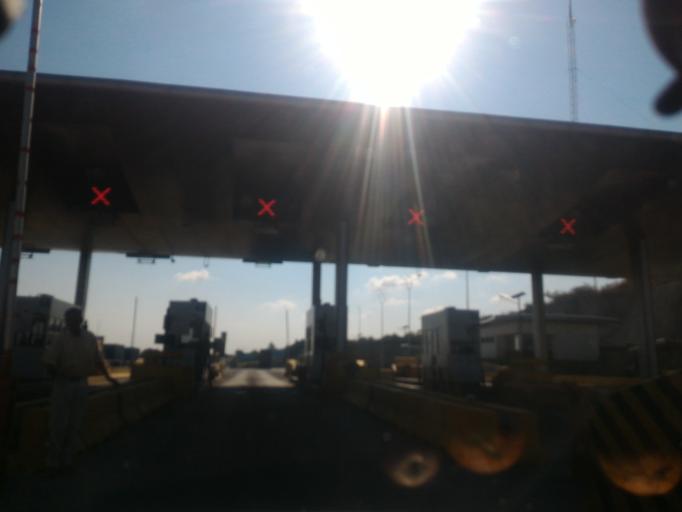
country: MX
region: Jalisco
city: Tonila
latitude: 19.4095
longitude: -103.5278
